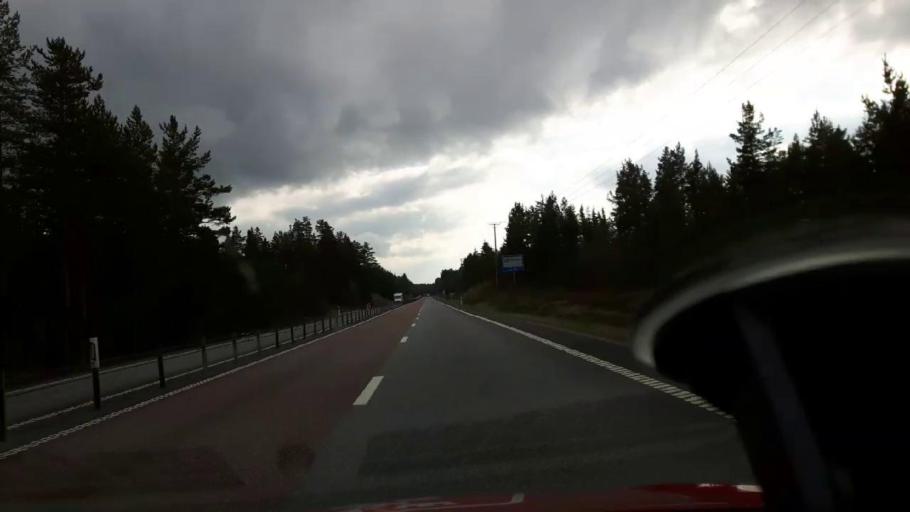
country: SE
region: Gaevleborg
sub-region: Gavle Kommun
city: Norrsundet
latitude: 61.0189
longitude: 16.9773
